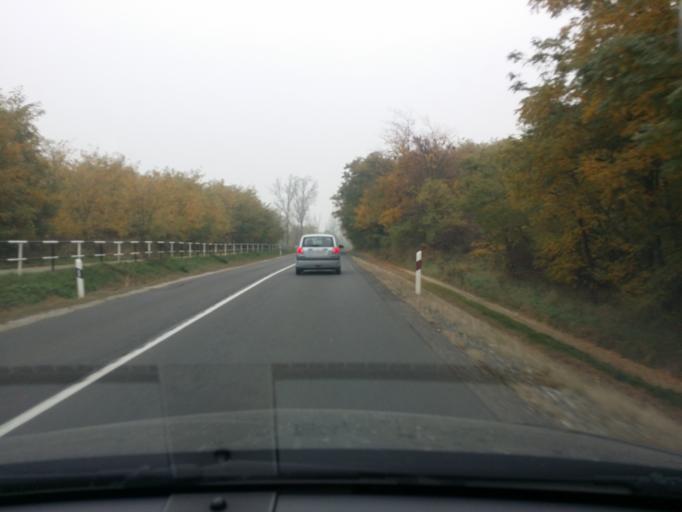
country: HU
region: Szabolcs-Szatmar-Bereg
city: Nyirpazony
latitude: 48.0025
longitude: 21.8199
